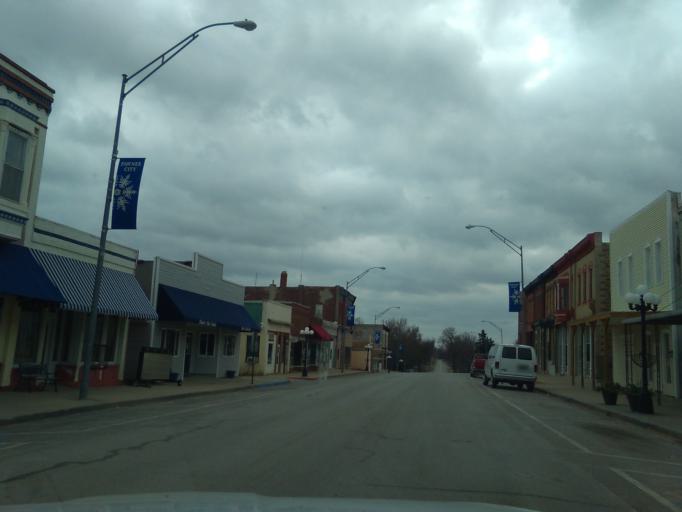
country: US
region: Nebraska
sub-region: Pawnee County
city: Pawnee City
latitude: 40.1094
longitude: -96.1529
